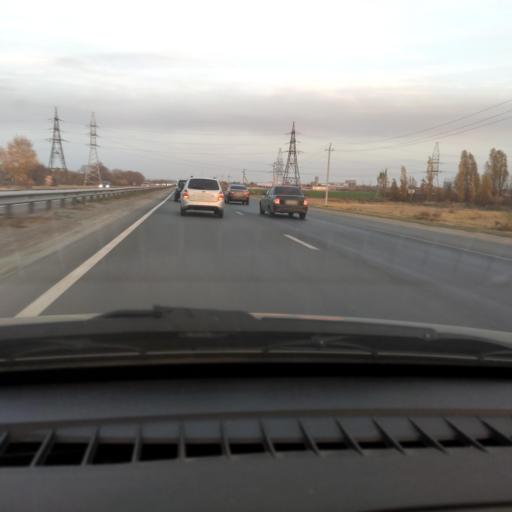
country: RU
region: Samara
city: Tol'yatti
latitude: 53.5766
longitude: 49.4293
